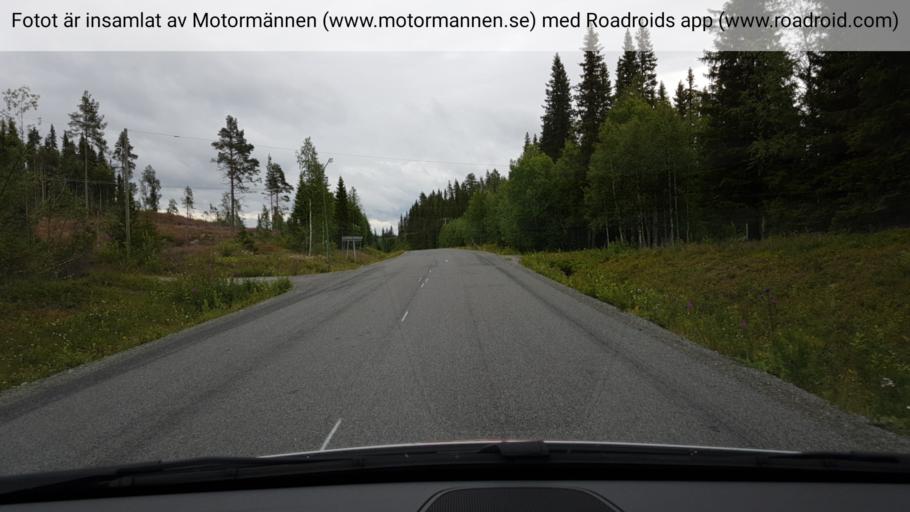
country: SE
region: Jaemtland
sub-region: Krokoms Kommun
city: Krokom
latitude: 63.6403
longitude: 14.3950
